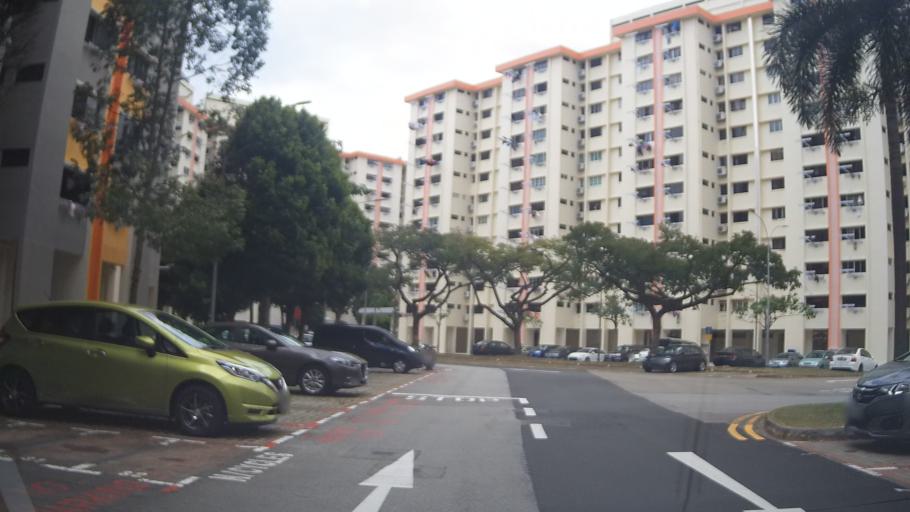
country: SG
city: Singapore
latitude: 1.3044
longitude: 103.7622
